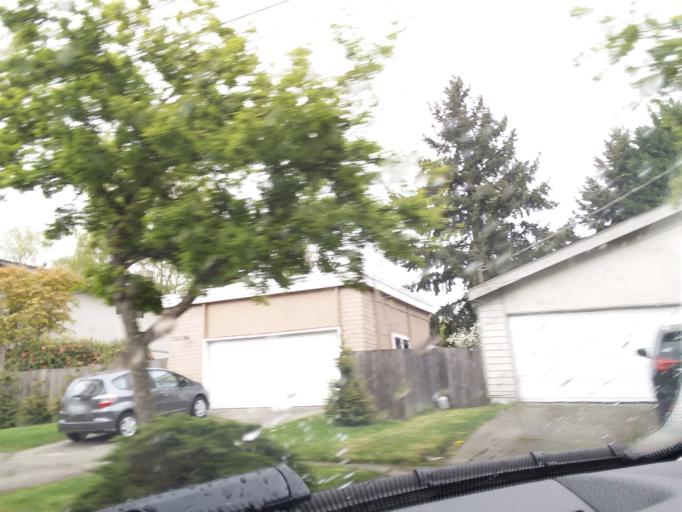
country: US
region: Washington
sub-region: King County
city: Lake Forest Park
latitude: 47.6810
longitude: -122.3007
